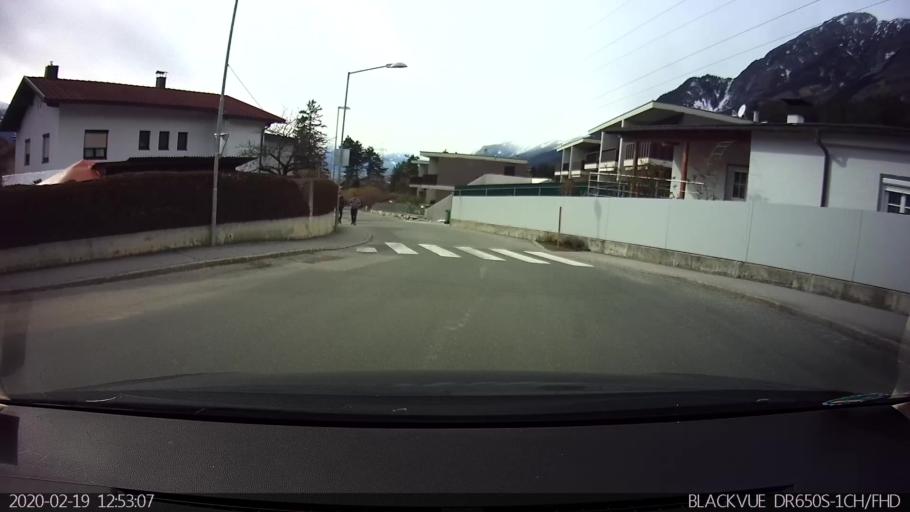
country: AT
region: Tyrol
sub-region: Politischer Bezirk Innsbruck Land
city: Absam
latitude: 47.3055
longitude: 11.5178
